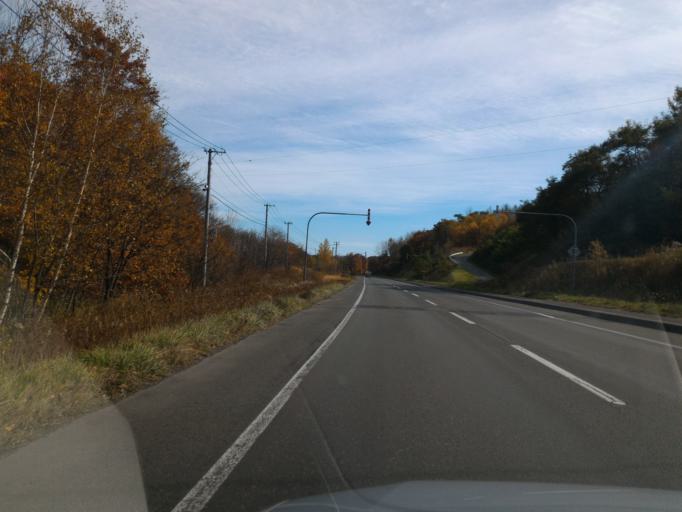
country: JP
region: Hokkaido
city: Shimo-furano
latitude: 43.3674
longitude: 142.3498
